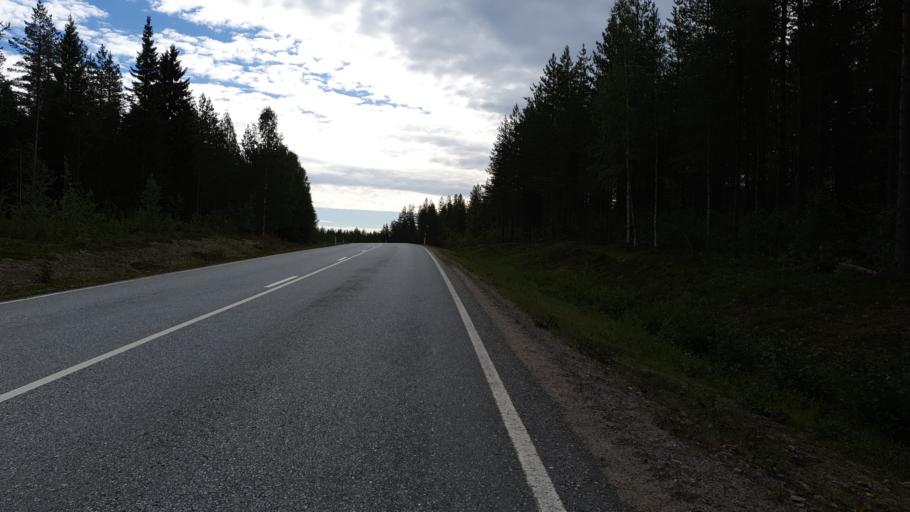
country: FI
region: Kainuu
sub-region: Kehys-Kainuu
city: Kuhmo
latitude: 64.4798
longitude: 29.7582
